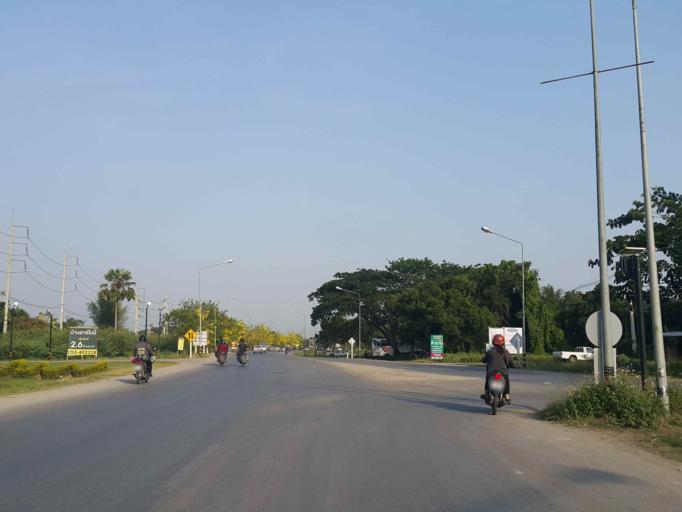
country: TH
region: Chiang Mai
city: San Sai
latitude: 18.8307
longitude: 99.0433
